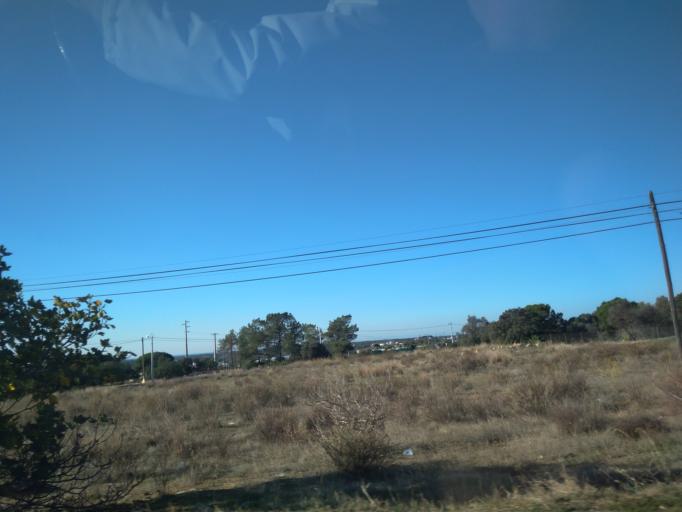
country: PT
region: Faro
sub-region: Faro
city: Santa Barbara de Nexe
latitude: 37.0887
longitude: -7.9597
